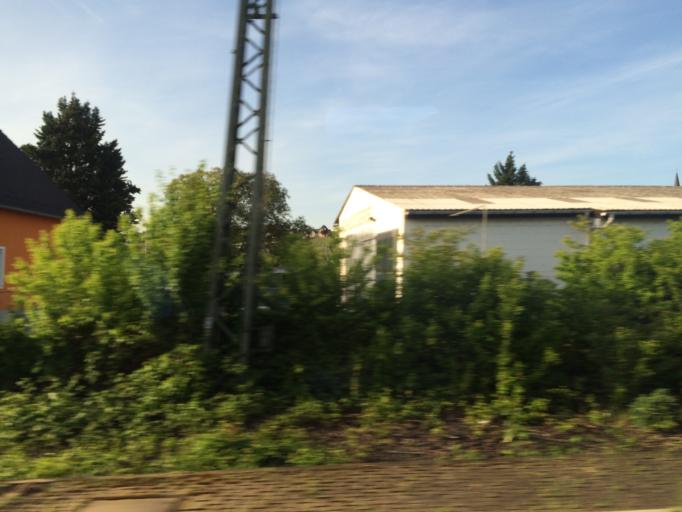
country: DE
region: Hesse
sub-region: Regierungsbezirk Darmstadt
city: Hochheim am Main
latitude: 50.0045
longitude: 8.3473
